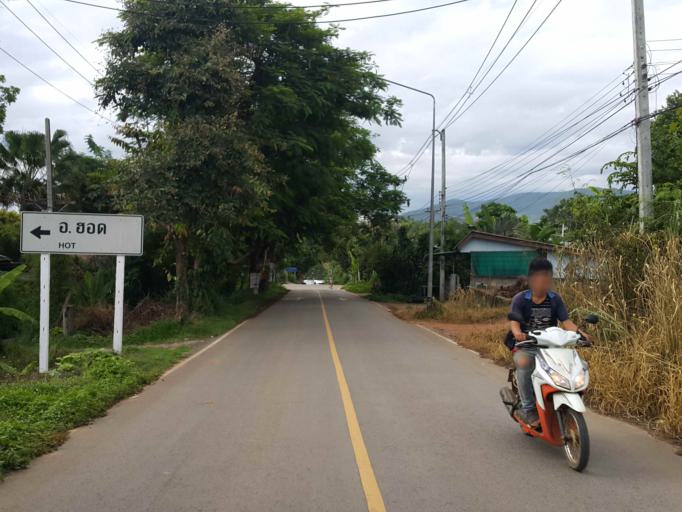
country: TH
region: Chiang Mai
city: Mae Chaem
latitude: 18.4875
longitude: 98.3776
